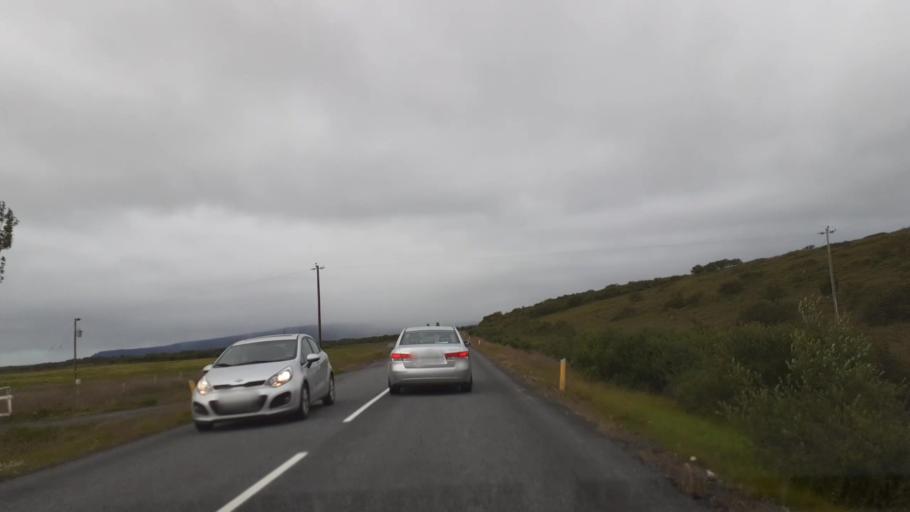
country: IS
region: Northeast
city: Husavik
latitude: 66.0674
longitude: -16.4409
